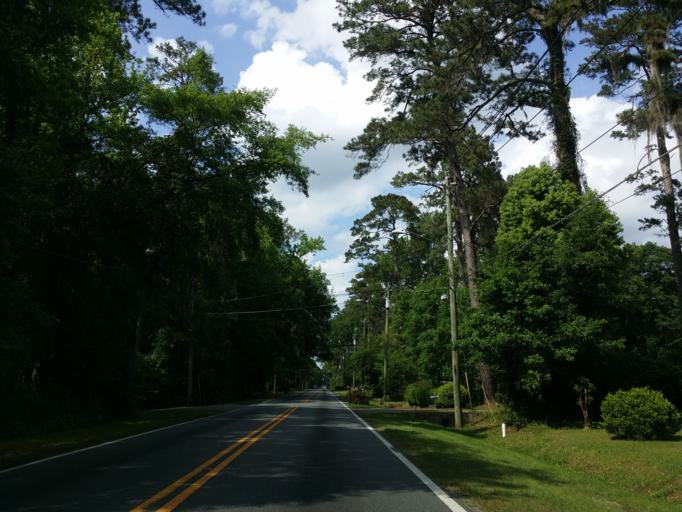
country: US
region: Florida
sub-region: Leon County
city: Tallahassee
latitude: 30.4254
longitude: -84.2620
